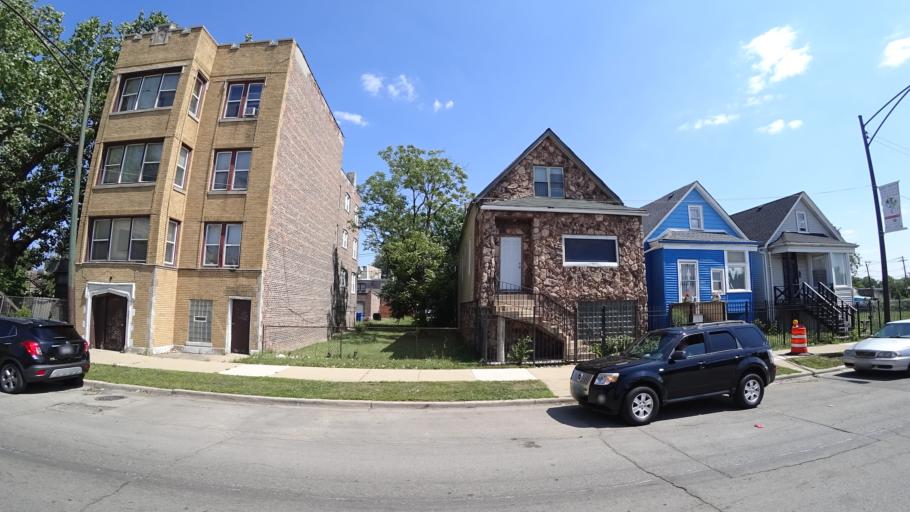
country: US
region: Illinois
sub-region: Cook County
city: Cicero
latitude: 41.8637
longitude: -87.7349
